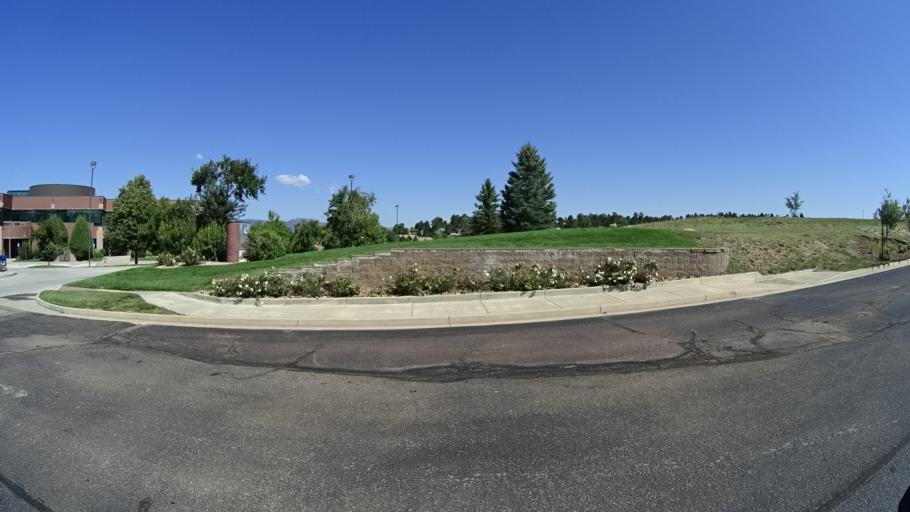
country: US
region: Colorado
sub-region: El Paso County
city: Air Force Academy
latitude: 38.9670
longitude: -104.7895
